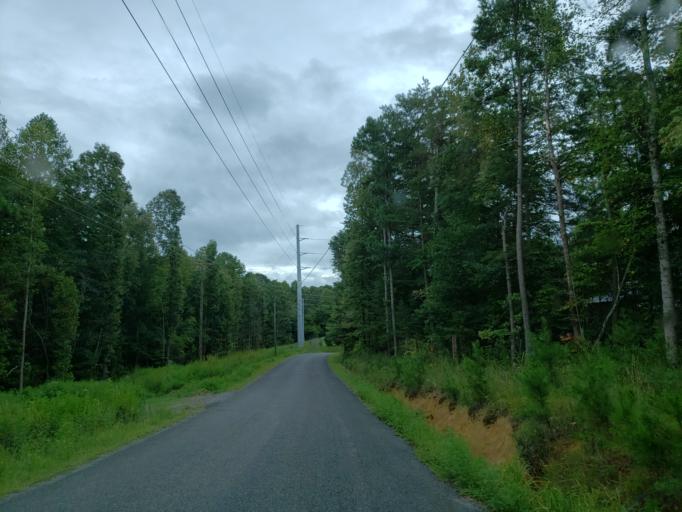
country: US
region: Georgia
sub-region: Gilmer County
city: Ellijay
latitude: 34.6176
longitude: -84.5709
